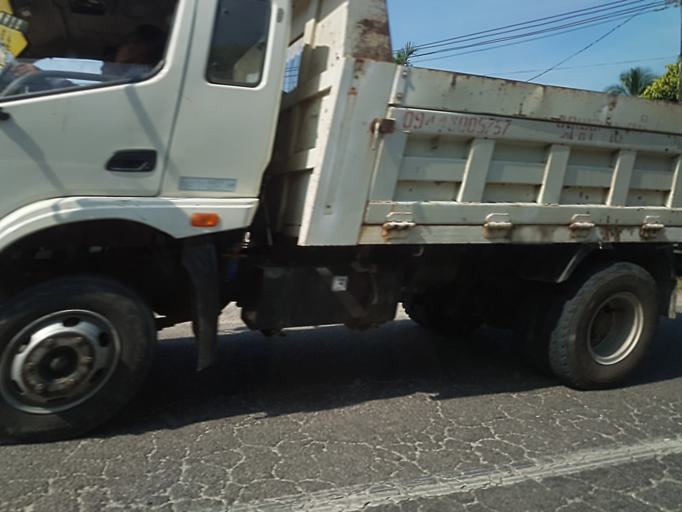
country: MM
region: Mon
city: Thaton
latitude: 16.6869
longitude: 97.4287
